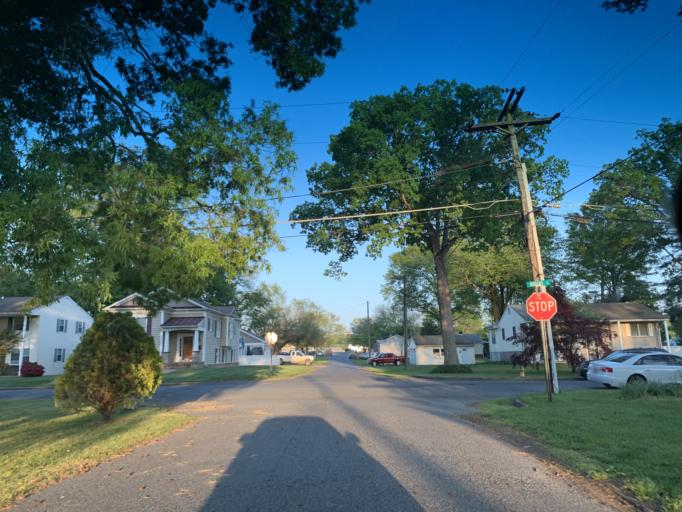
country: US
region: Maryland
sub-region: Harford County
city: Aberdeen
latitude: 39.5040
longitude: -76.1711
